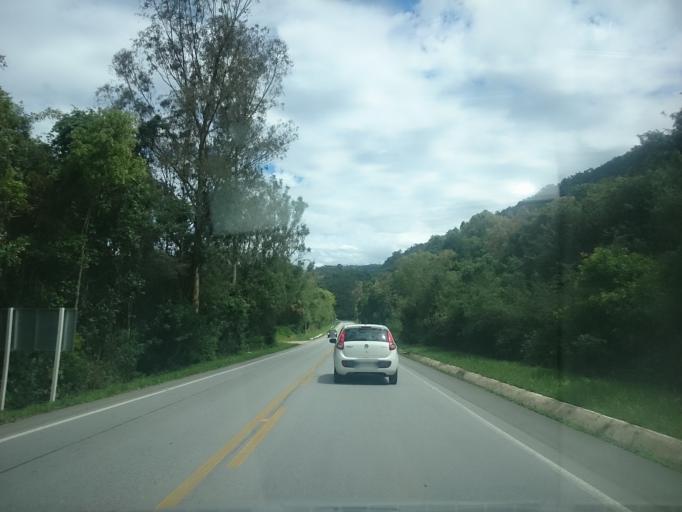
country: BR
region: Santa Catarina
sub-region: Anitapolis
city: Anitapolis
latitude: -27.6963
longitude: -49.2347
